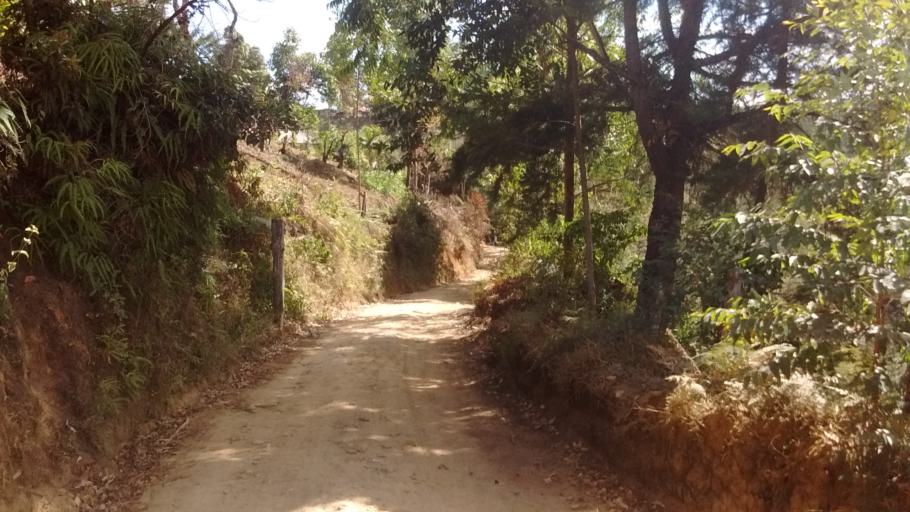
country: CO
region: Cauca
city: Popayan
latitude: 2.4607
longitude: -76.5697
